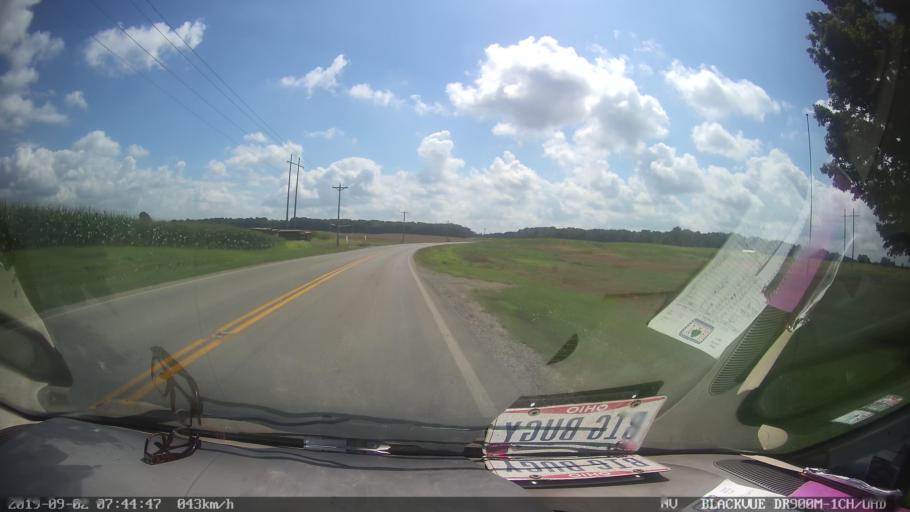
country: US
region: Ohio
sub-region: Knox County
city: Centerburg
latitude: 40.4237
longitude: -82.6983
